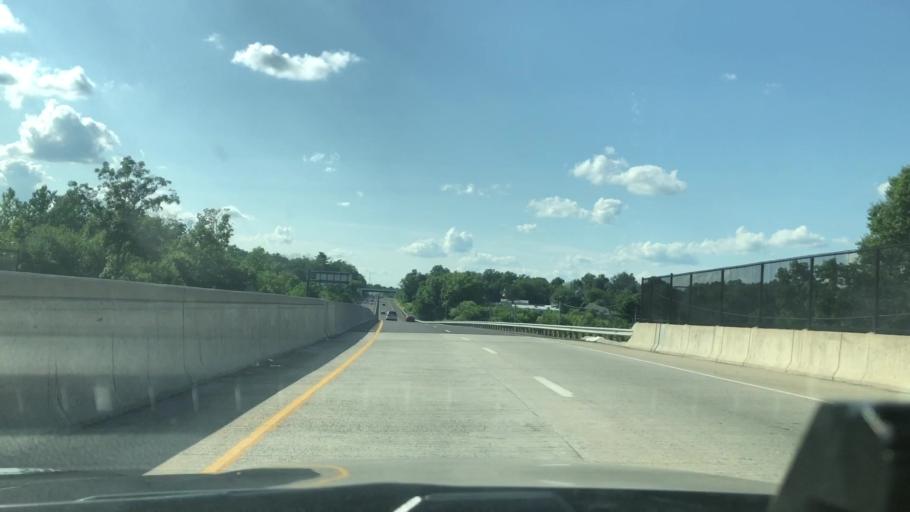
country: US
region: Pennsylvania
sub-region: Montgomery County
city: Spring House
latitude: 40.1904
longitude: -75.2150
